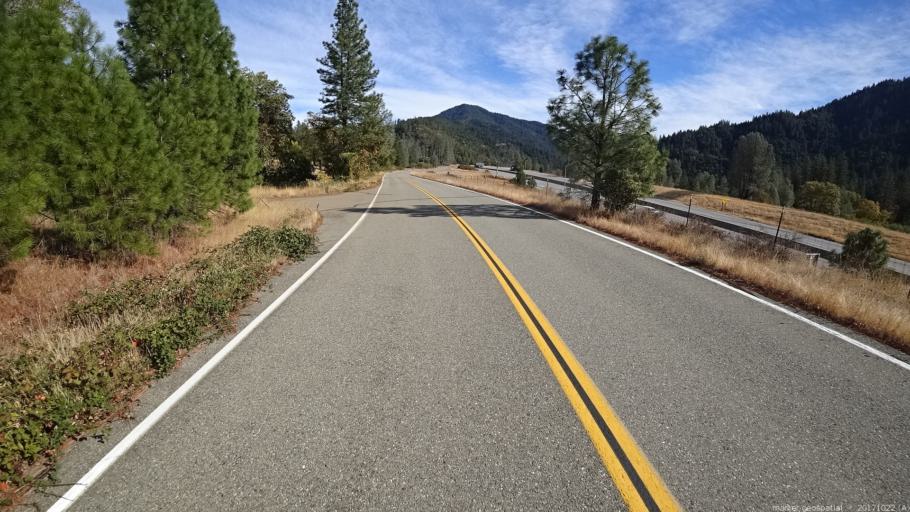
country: US
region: California
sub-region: Siskiyou County
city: Dunsmuir
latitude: 41.0004
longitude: -122.4140
